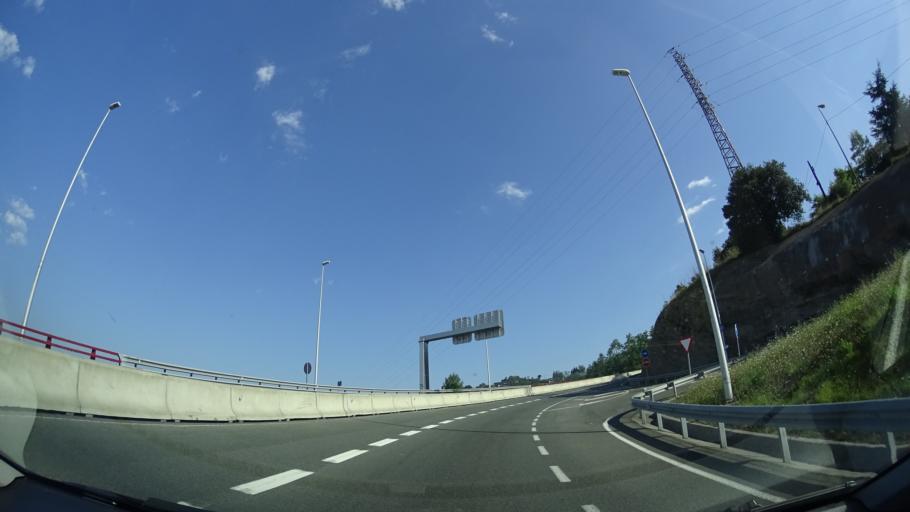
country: ES
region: Basque Country
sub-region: Bizkaia
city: Santutxu
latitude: 43.2655
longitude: -2.9080
